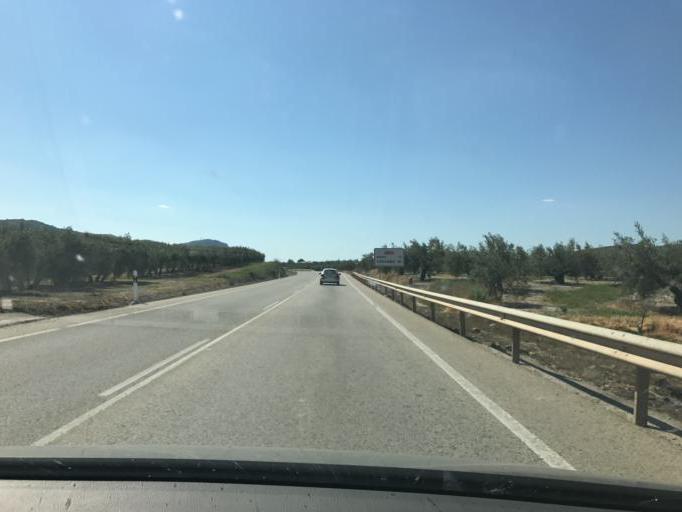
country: ES
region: Andalusia
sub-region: Province of Cordoba
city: Luque
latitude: 37.5642
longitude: -4.2159
